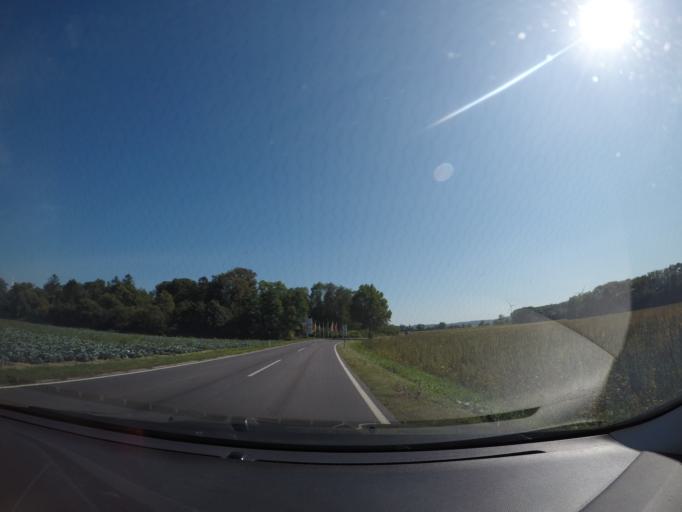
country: AT
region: Lower Austria
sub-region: Politischer Bezirk Baden
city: Seibersdorf
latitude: 47.9575
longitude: 16.5341
